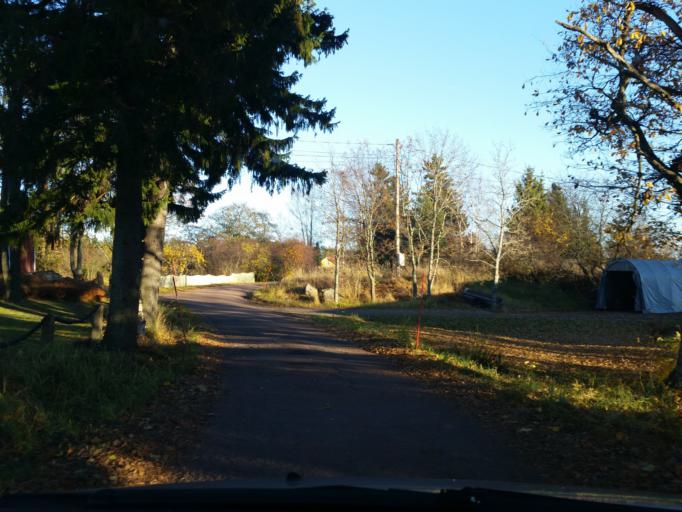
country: AX
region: Alands skaergard
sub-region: Braendoe
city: Braendoe
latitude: 60.3574
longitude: 21.0652
